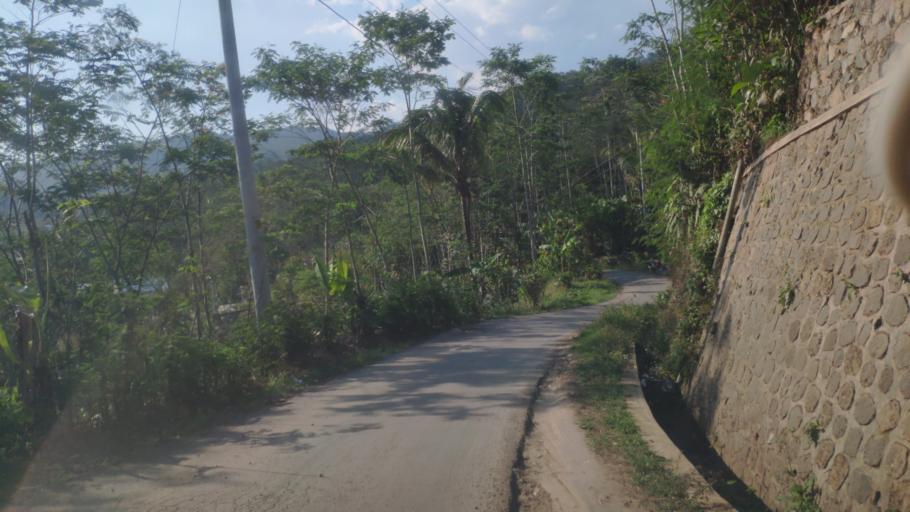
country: ID
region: Central Java
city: Buaran
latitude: -7.2430
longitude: 109.5872
